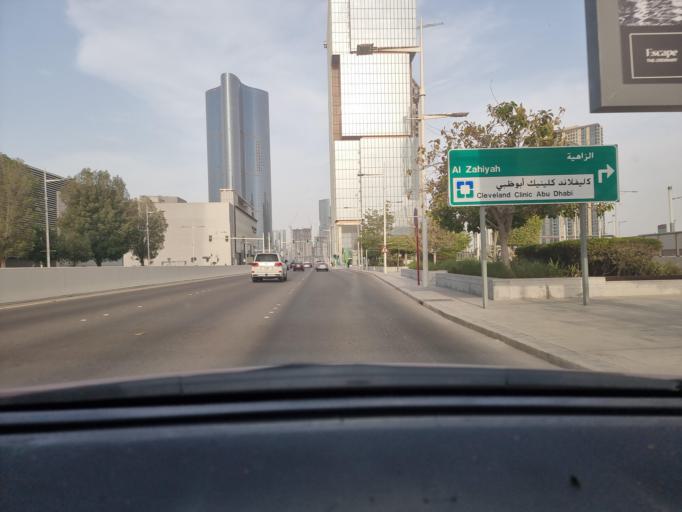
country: AE
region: Abu Dhabi
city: Abu Dhabi
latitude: 24.4989
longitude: 54.3883
